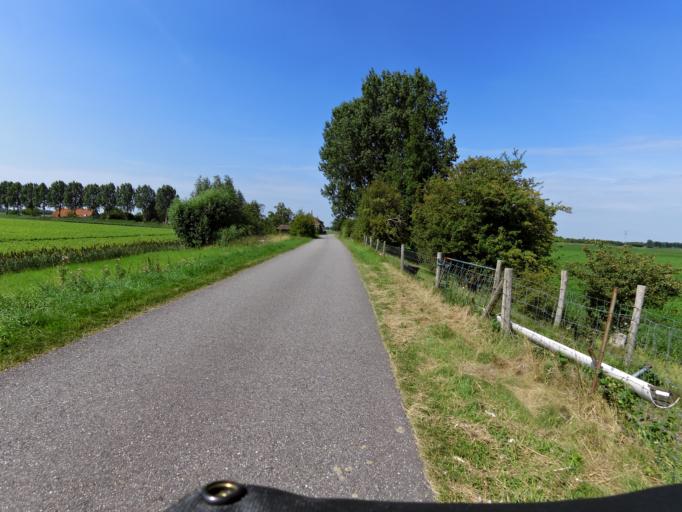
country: NL
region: North Brabant
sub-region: Gemeente Steenbergen
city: Dinteloord
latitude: 51.6932
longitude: 4.2970
